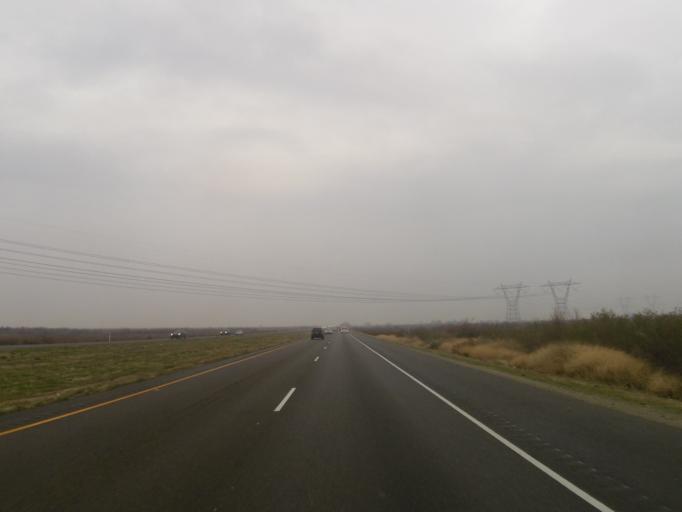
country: US
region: California
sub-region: Kern County
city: Greenfield
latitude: 35.1020
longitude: -119.0449
